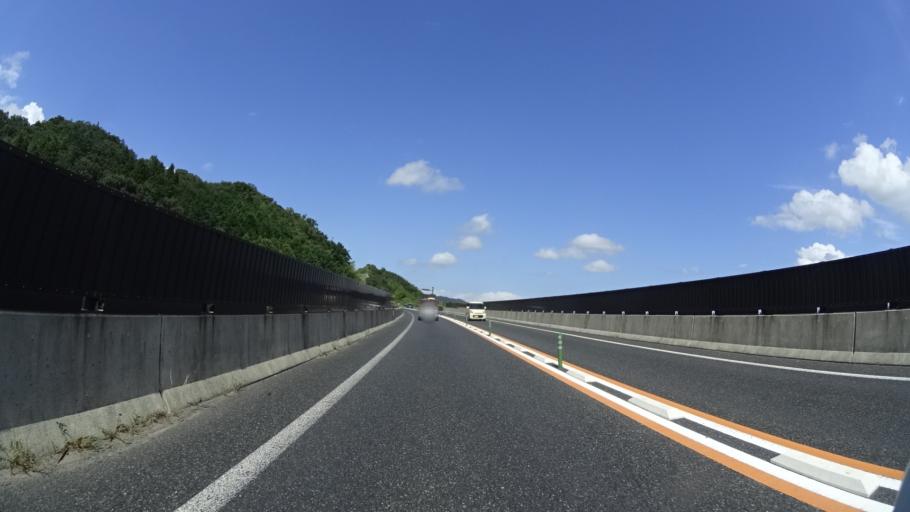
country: JP
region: Tottori
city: Tottori
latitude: 35.4390
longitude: 134.2034
